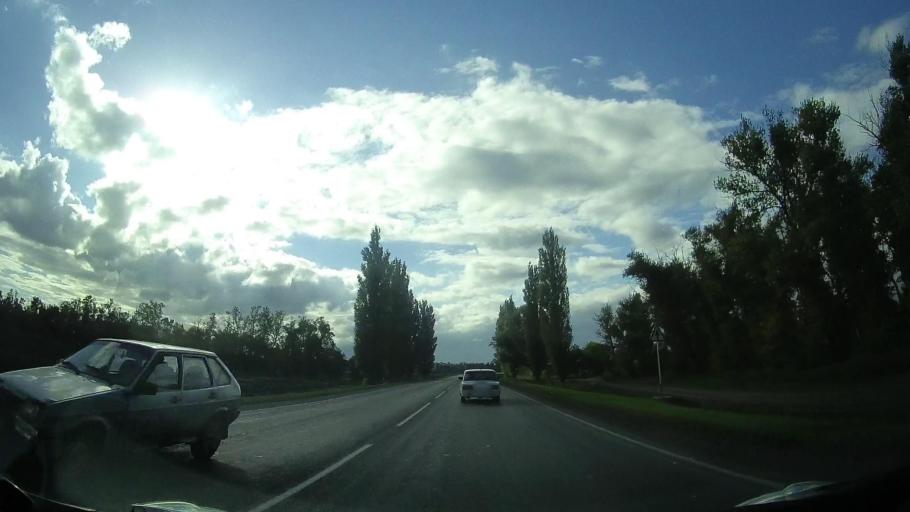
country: RU
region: Rostov
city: Tselina
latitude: 46.5306
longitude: 40.9559
